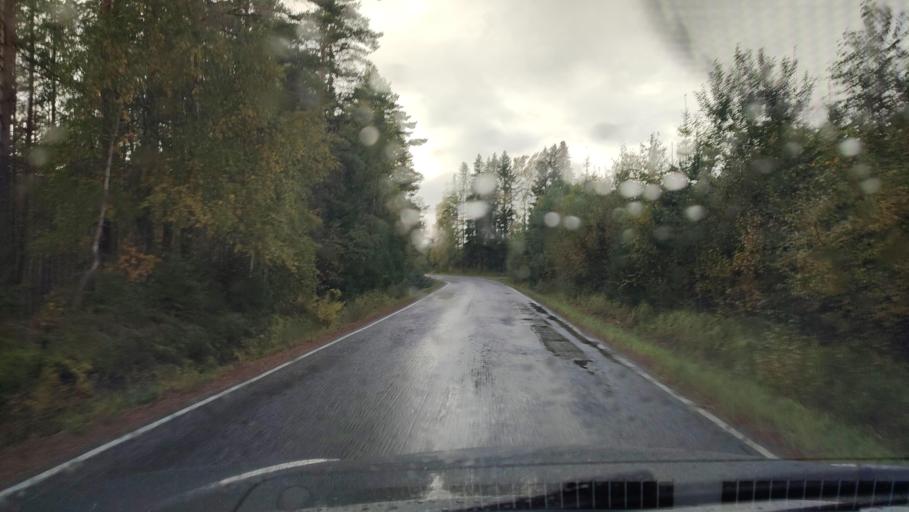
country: FI
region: Southern Ostrobothnia
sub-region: Suupohja
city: Karijoki
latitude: 62.3285
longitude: 21.6649
